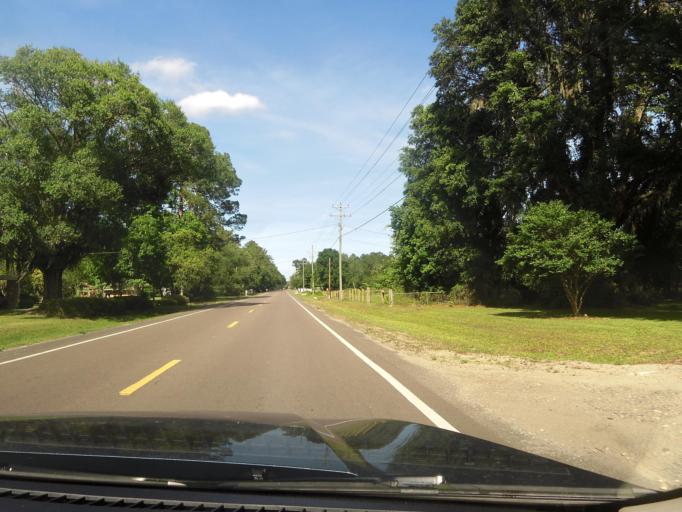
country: US
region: Florida
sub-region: Nassau County
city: Callahan
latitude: 30.5585
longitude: -81.8633
